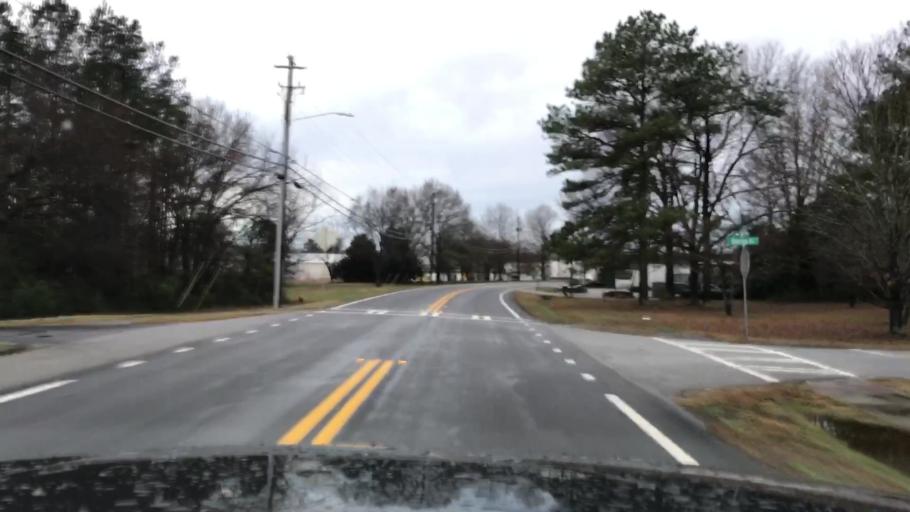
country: US
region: Georgia
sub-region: Morgan County
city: Madison
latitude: 33.5833
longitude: -83.4806
